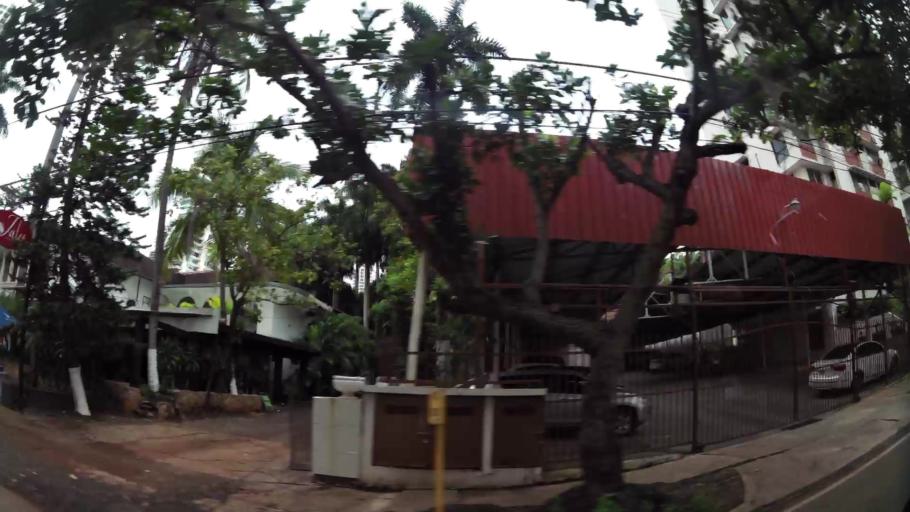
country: PA
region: Panama
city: Panama
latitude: 8.9769
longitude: -79.5276
